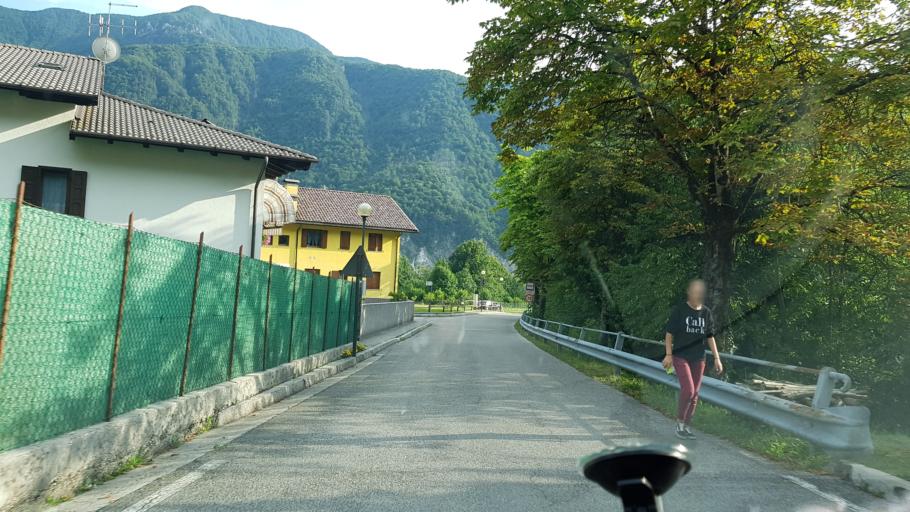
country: IT
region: Friuli Venezia Giulia
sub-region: Provincia di Udine
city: Prato
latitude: 46.3629
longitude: 13.3508
